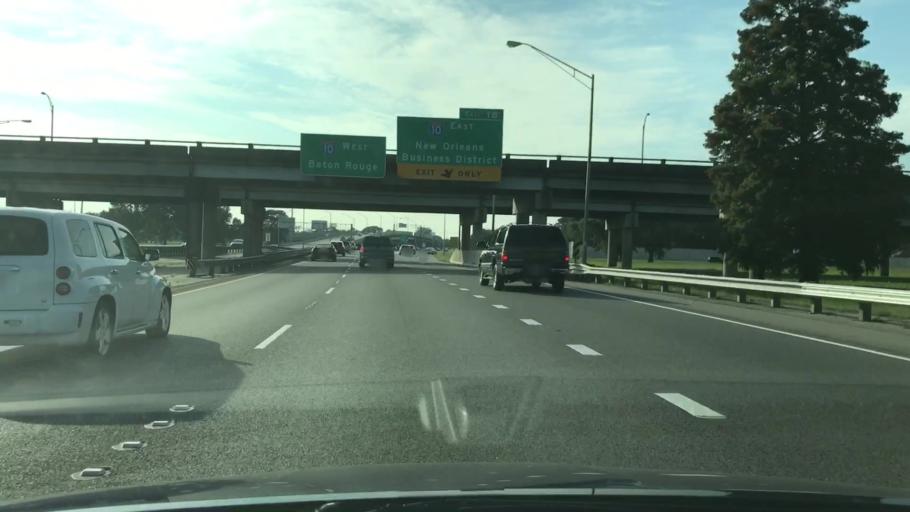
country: US
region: Louisiana
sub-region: Jefferson Parish
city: Metairie
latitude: 29.9958
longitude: -90.1149
